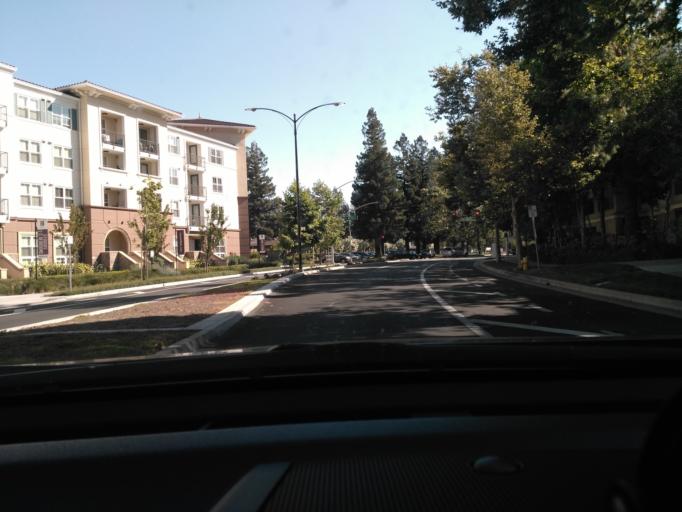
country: US
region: California
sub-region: Santa Clara County
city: Milpitas
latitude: 37.3997
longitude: -121.9216
